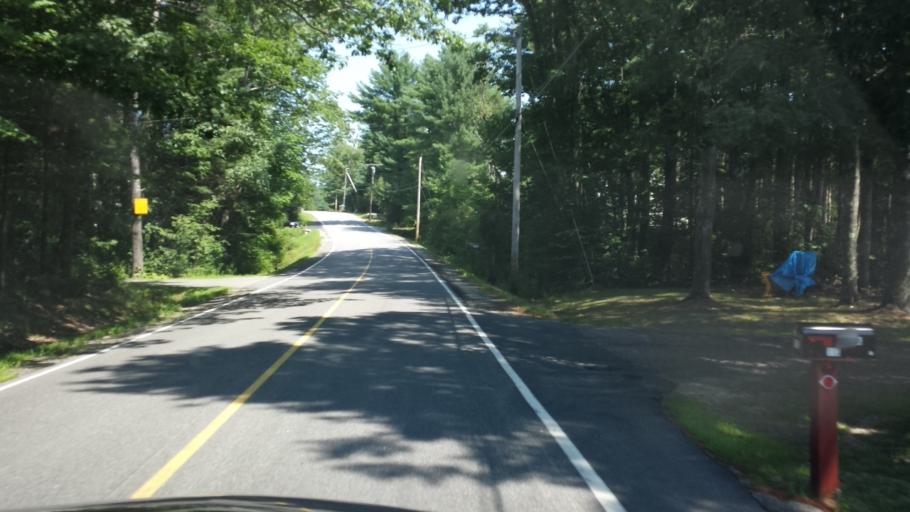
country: US
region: Maine
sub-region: York County
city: Biddeford
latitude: 43.4638
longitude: -70.5072
